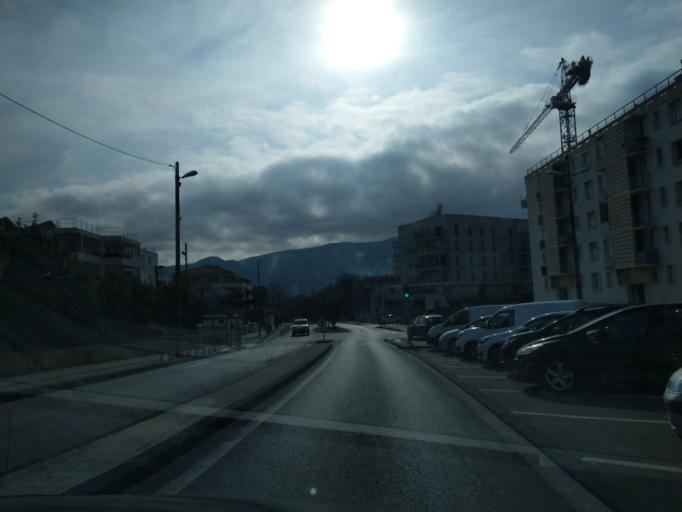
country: FR
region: Provence-Alpes-Cote d'Azur
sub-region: Departement des Bouches-du-Rhone
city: Marseille 12
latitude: 43.2983
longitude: 5.4402
